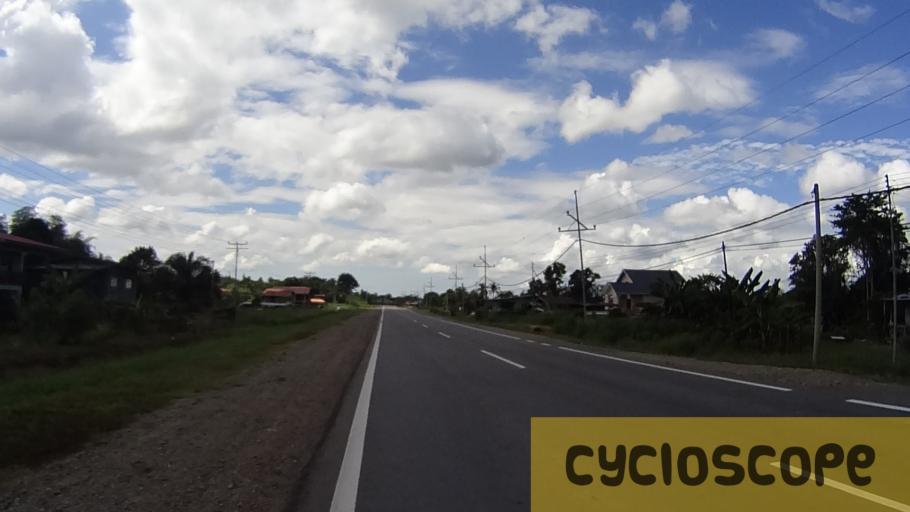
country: MY
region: Sabah
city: Beaufort
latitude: 5.2956
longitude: 115.6911
